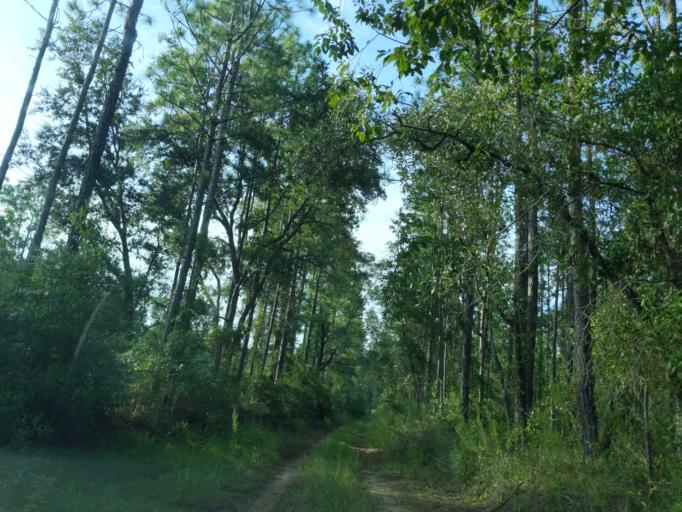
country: US
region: Florida
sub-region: Leon County
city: Tallahassee
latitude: 30.3562
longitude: -84.3611
